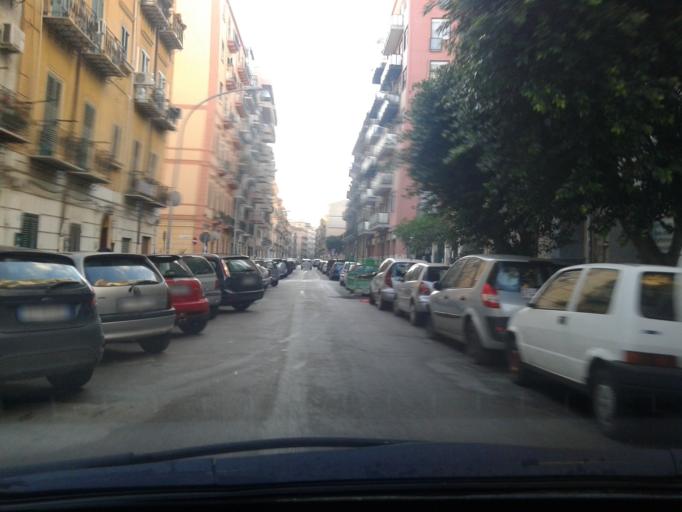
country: IT
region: Sicily
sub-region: Palermo
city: Palermo
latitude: 38.1215
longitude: 13.3441
